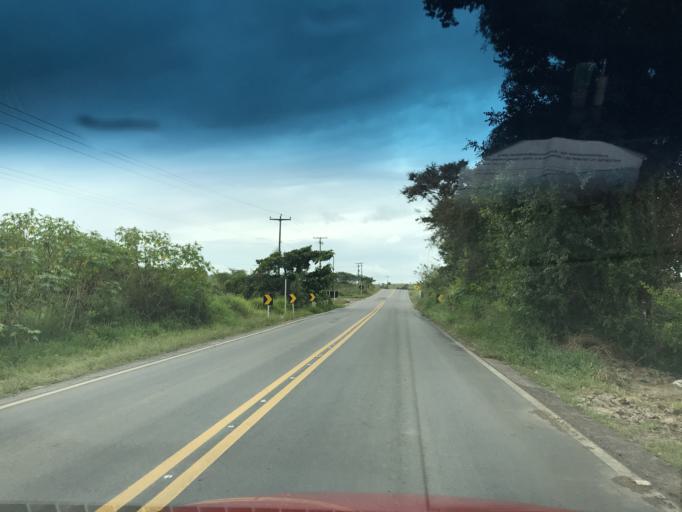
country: BR
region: Bahia
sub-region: Castro Alves
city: Castro Alves
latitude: -12.7589
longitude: -39.4179
